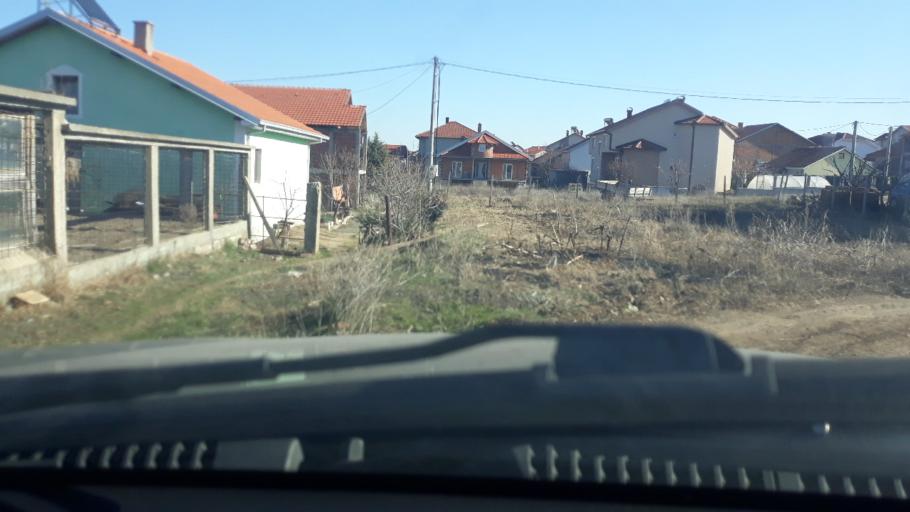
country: MK
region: Sveti Nikole
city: Sveti Nikole
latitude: 41.8725
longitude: 21.9326
